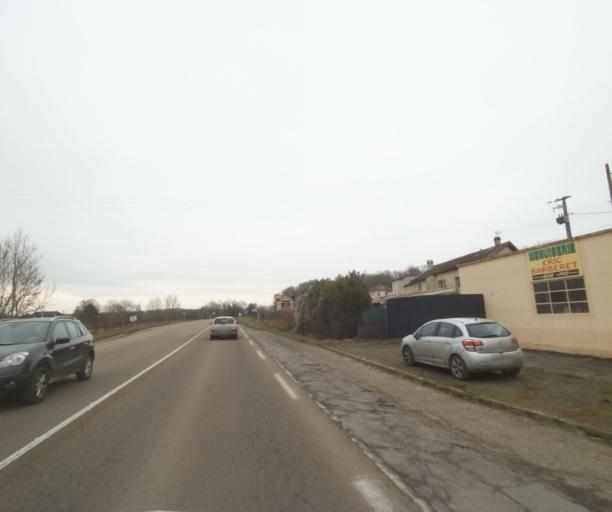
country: FR
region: Champagne-Ardenne
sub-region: Departement de la Haute-Marne
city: Bienville
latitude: 48.6035
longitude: 5.0304
